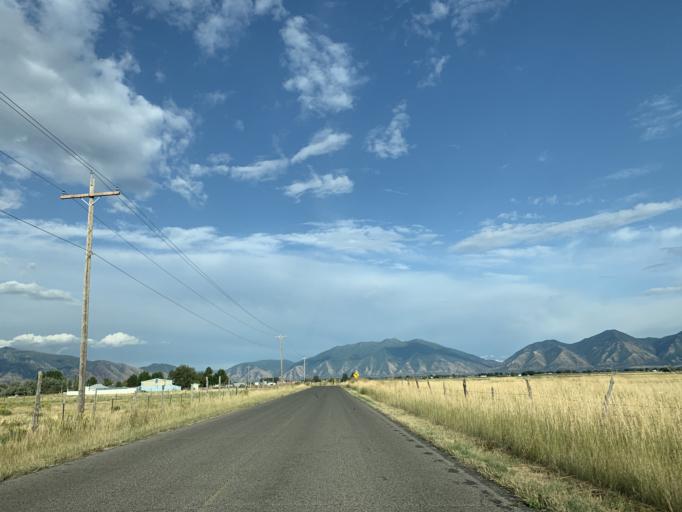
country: US
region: Utah
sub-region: Utah County
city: West Mountain
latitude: 40.1142
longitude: -111.7827
